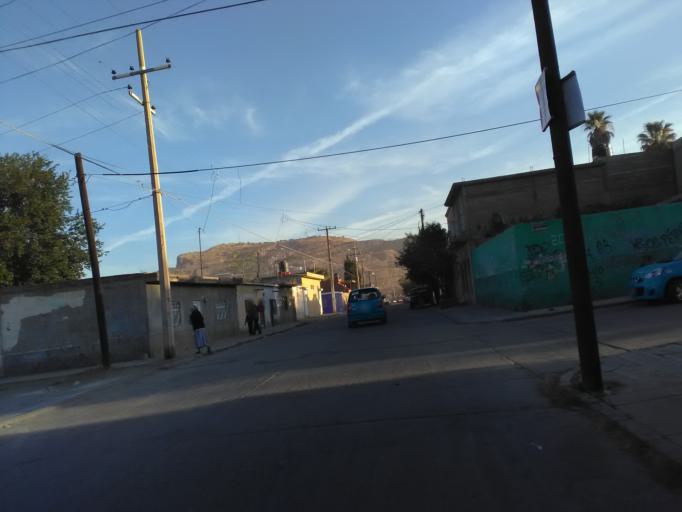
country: MX
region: Durango
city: Victoria de Durango
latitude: 24.0441
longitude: -104.6686
